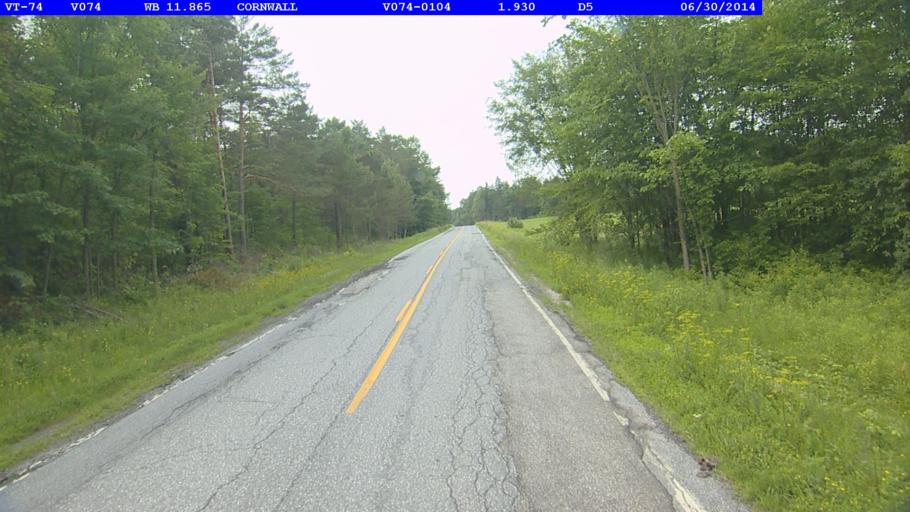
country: US
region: Vermont
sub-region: Addison County
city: Middlebury (village)
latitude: 43.9507
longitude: -73.2234
